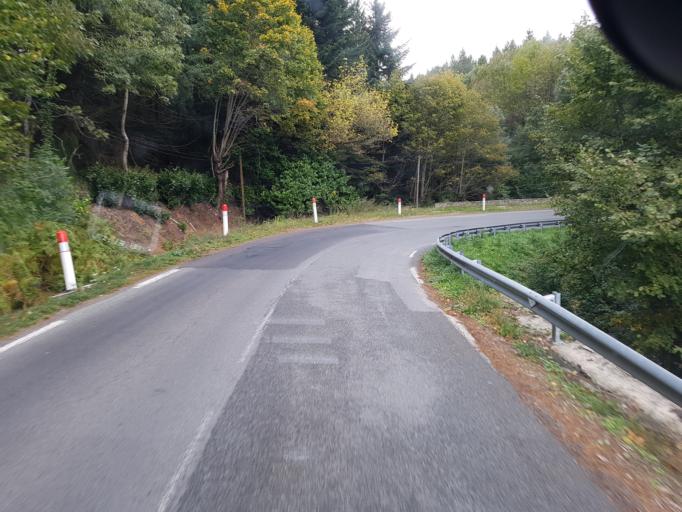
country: FR
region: Languedoc-Roussillon
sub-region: Departement de l'Aude
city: Cuxac-Cabardes
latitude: 43.4052
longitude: 2.2979
